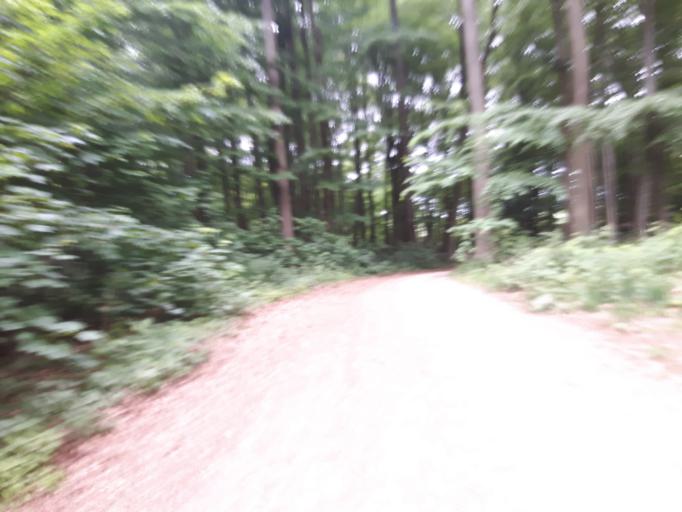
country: DE
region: Schleswig-Holstein
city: Schashagen
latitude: 54.1148
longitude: 10.9189
